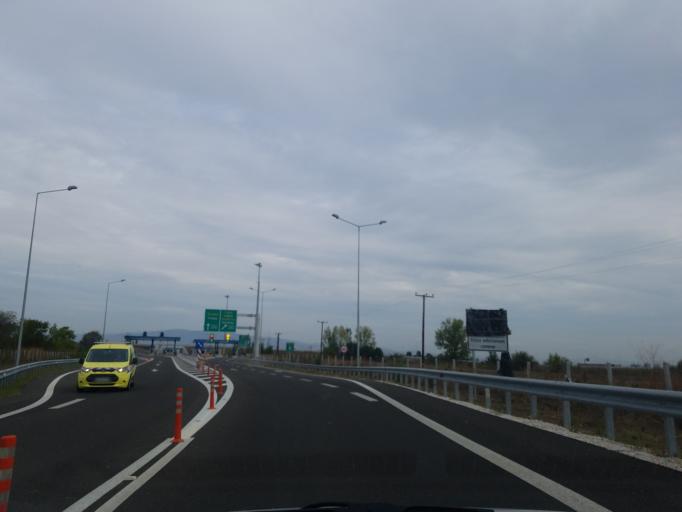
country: GR
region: Thessaly
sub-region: Nomos Kardhitsas
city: Agia Triada
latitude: 39.4726
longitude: 21.9030
